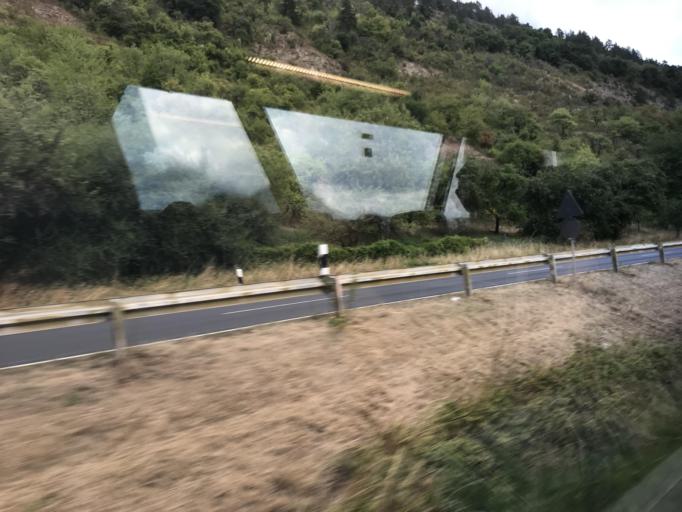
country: DE
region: Bavaria
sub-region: Regierungsbezirk Unterfranken
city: Hammelburg
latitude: 50.1244
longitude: 9.9131
